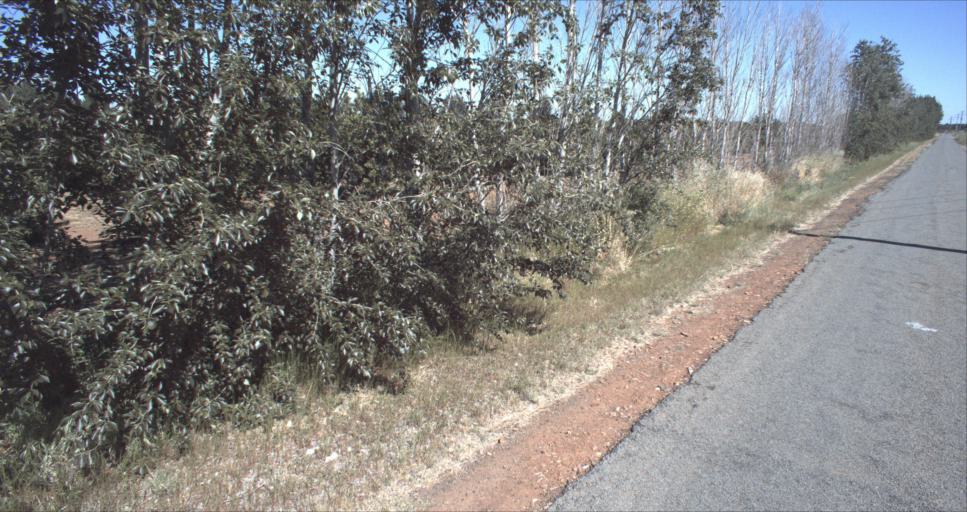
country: AU
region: New South Wales
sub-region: Leeton
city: Leeton
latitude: -34.5424
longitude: 146.3428
